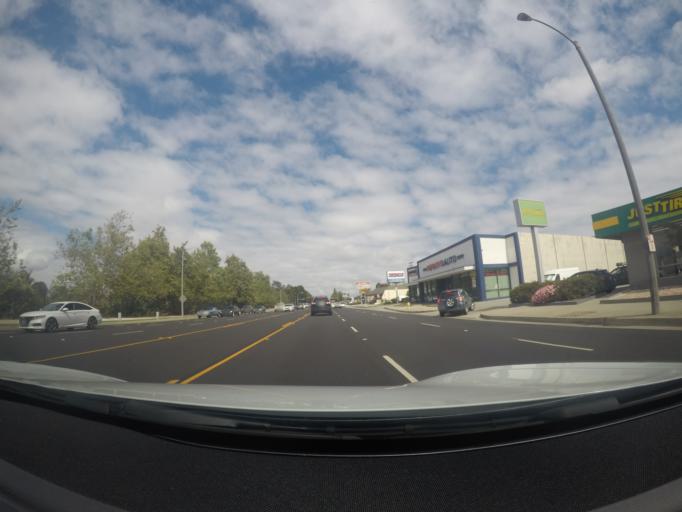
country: US
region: California
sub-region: Los Angeles County
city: Torrance
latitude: 33.8247
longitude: -118.3425
